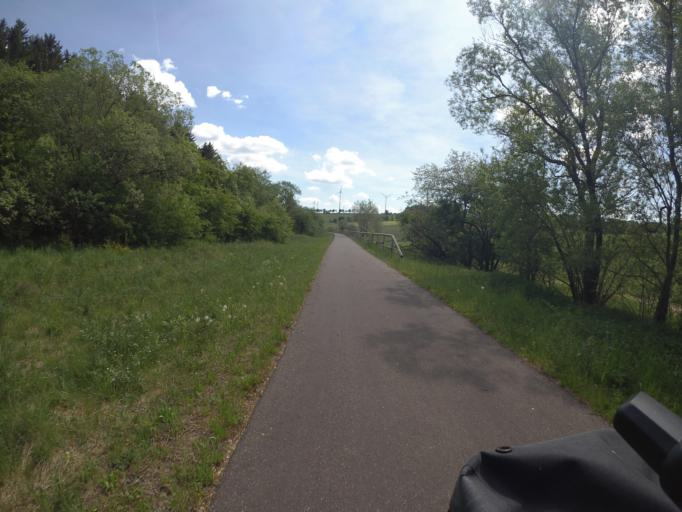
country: DE
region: Rheinland-Pfalz
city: Scheid
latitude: 50.3527
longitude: 6.4140
